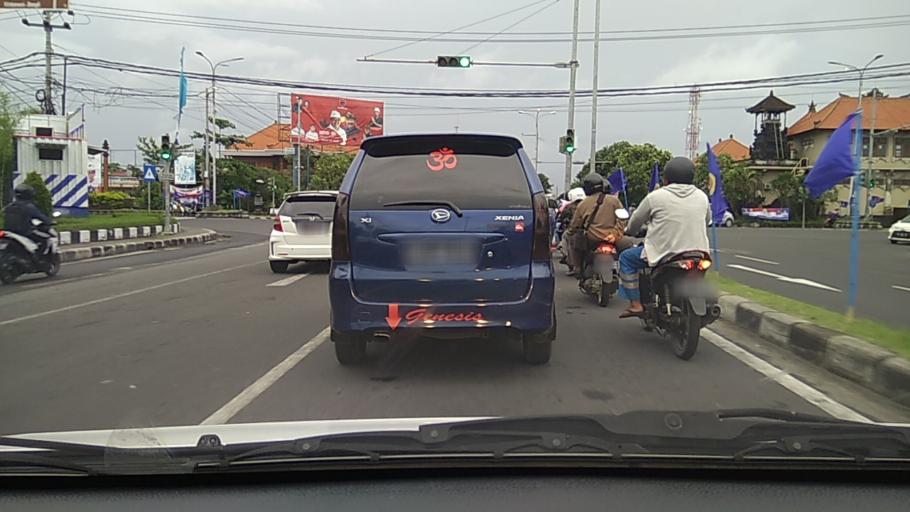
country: ID
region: Bali
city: Karyadharma
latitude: -8.7176
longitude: 115.2150
